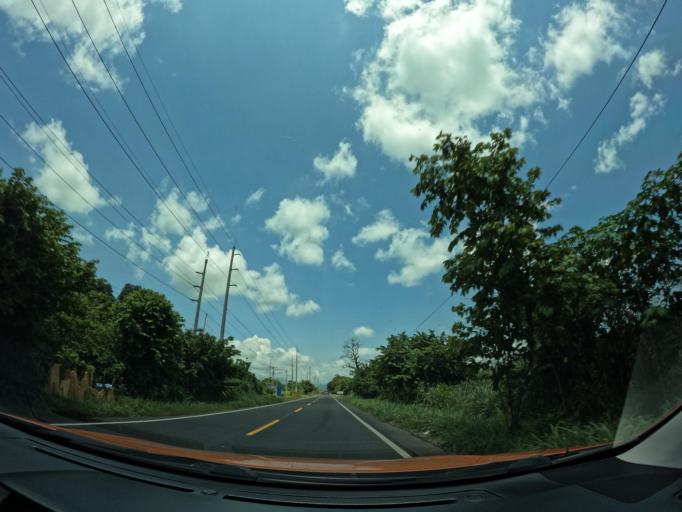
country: GT
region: Escuintla
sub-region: Municipio de Masagua
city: Masagua
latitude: 14.2316
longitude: -90.8235
